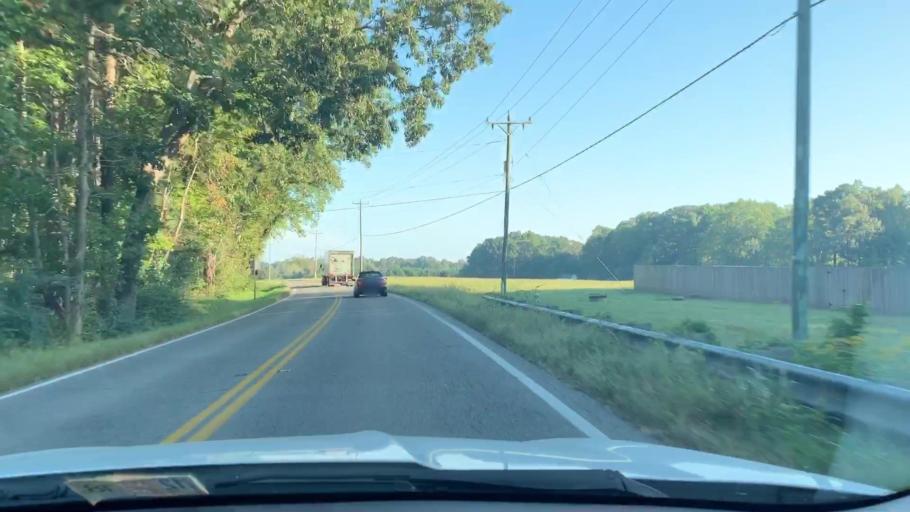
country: US
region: Virginia
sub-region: Middlesex County
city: Deltaville
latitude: 37.5300
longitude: -76.4216
